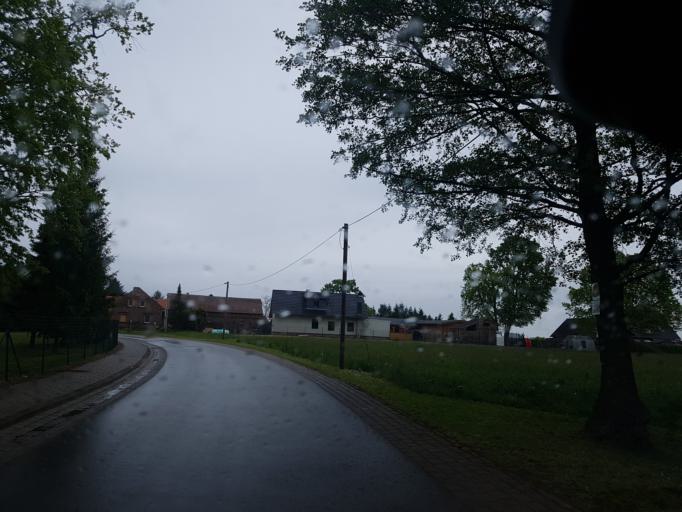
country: DE
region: Saxony
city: Gross Duben
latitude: 51.6672
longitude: 14.4740
